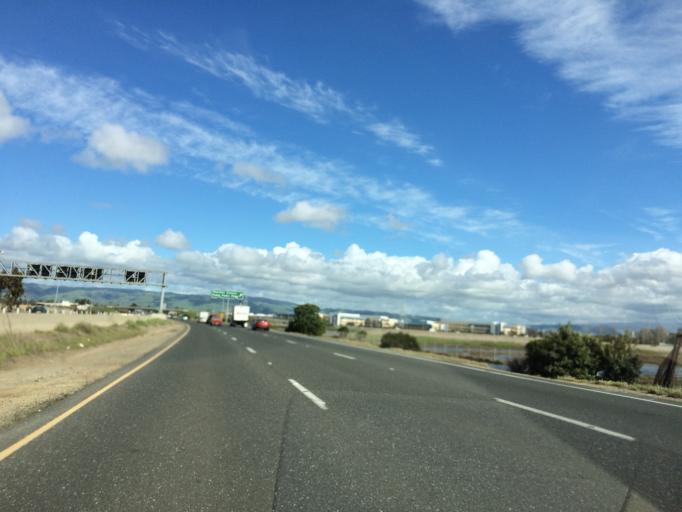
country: US
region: California
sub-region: Alameda County
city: Newark
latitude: 37.5363
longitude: -122.0729
